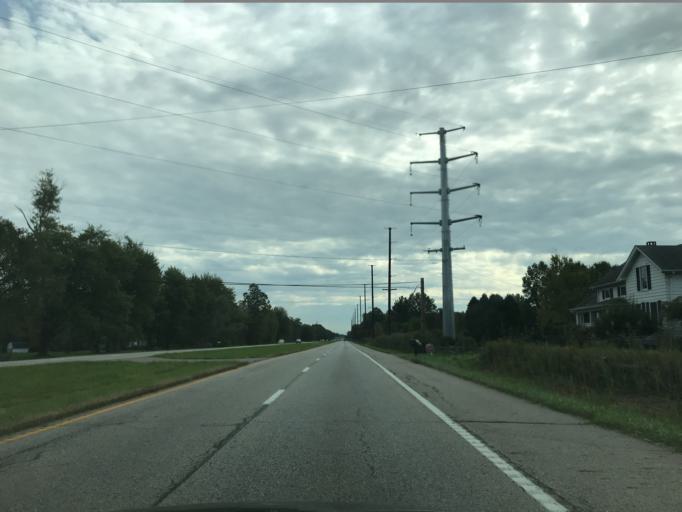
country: US
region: Ohio
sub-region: Trumbull County
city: Leavittsburg
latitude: 41.2744
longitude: -80.9005
